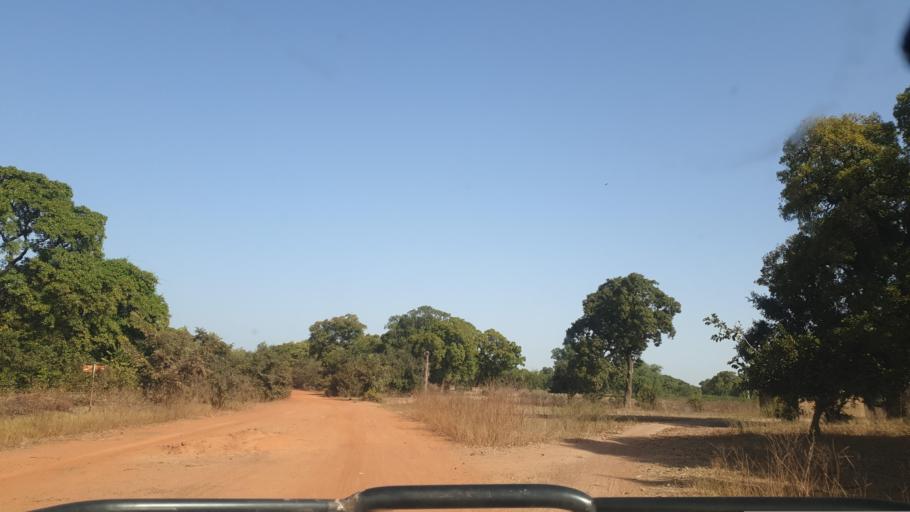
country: ML
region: Sikasso
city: Bougouni
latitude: 11.7704
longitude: -6.9025
